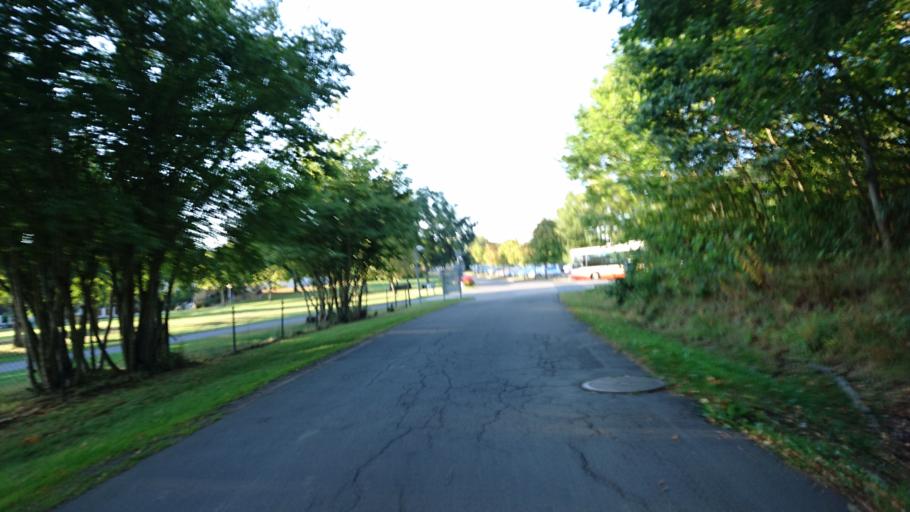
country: SE
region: Joenkoeping
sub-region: Jonkopings Kommun
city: Jonkoping
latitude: 57.8157
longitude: 14.1516
